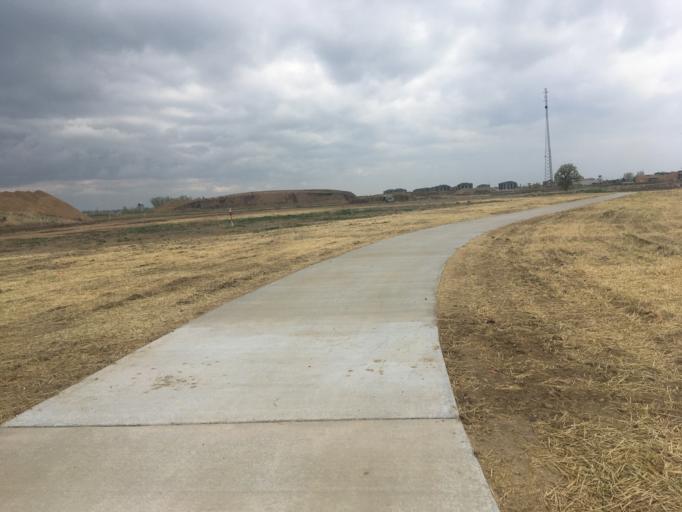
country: US
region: Colorado
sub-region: Weld County
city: Mead
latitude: 40.1750
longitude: -104.9733
